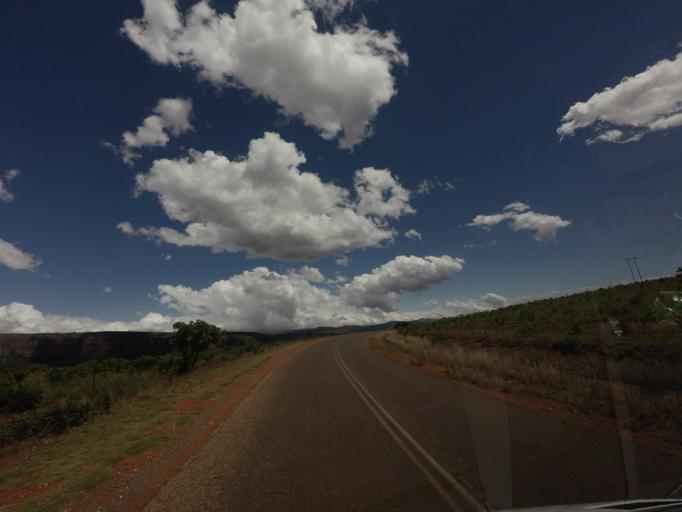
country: ZA
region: Limpopo
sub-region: Mopani District Municipality
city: Hoedspruit
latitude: -24.6170
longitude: 30.8191
